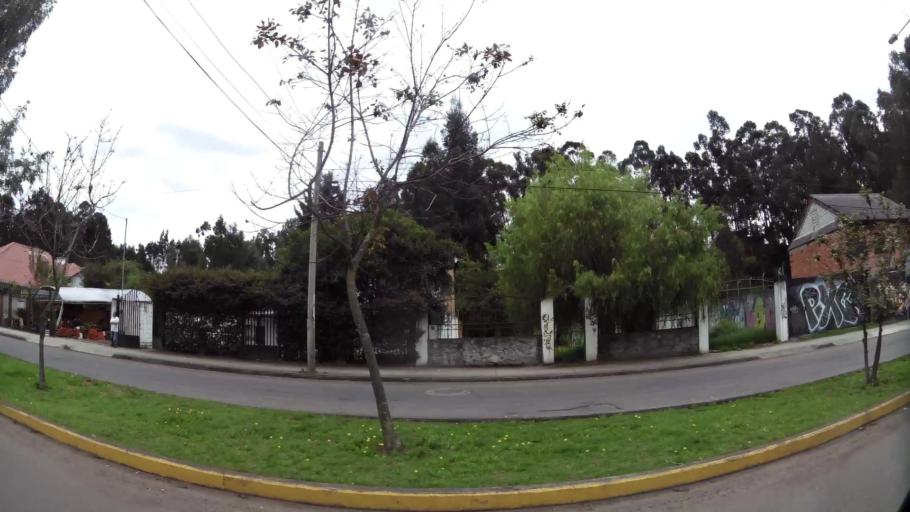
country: EC
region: Azuay
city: Cuenca
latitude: -2.9070
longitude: -79.0256
